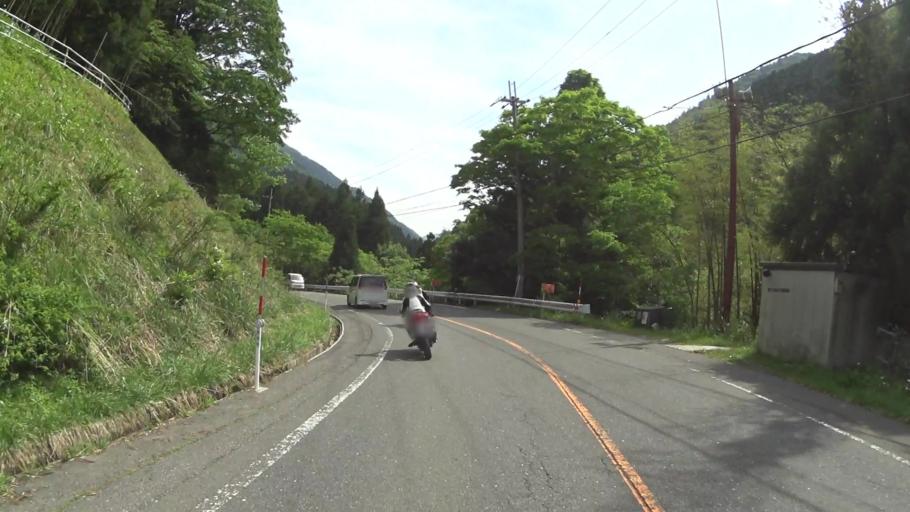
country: JP
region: Shiga Prefecture
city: Kitahama
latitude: 35.2816
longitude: 135.8799
